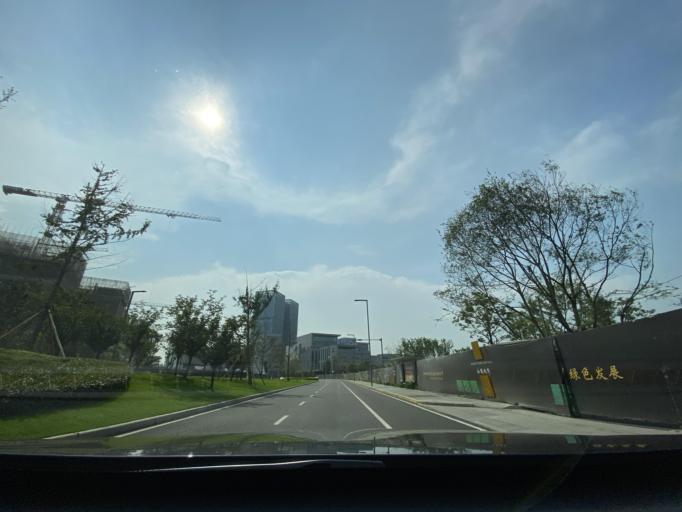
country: CN
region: Sichuan
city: Dongsheng
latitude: 30.3950
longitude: 104.0763
